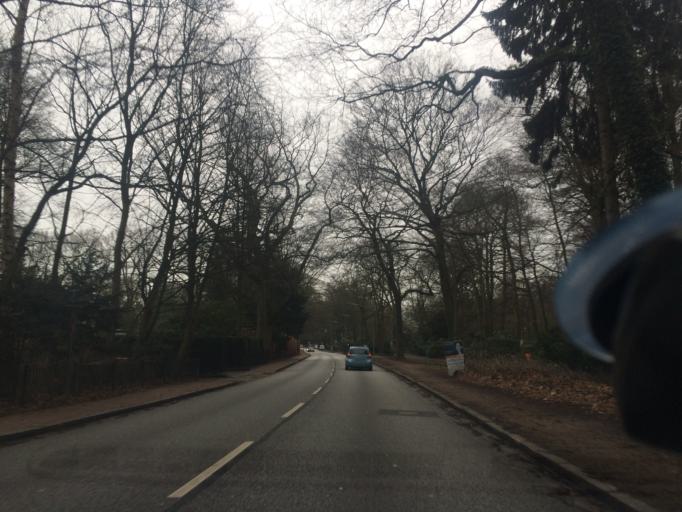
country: DE
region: Schleswig-Holstein
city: Halstenbek
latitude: 53.5572
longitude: 9.8309
